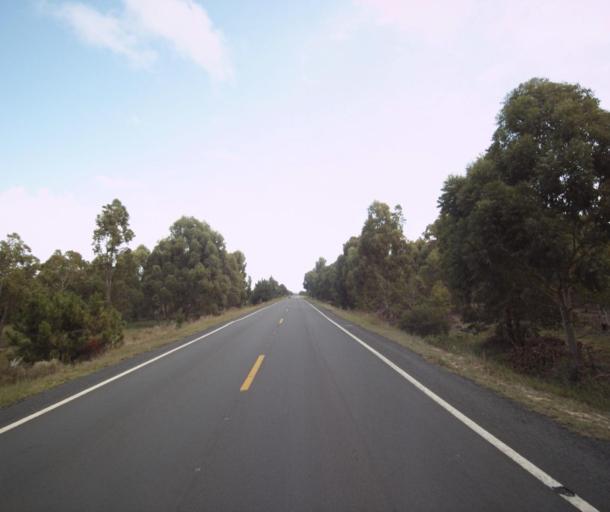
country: BR
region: Rio Grande do Sul
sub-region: Tapes
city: Tapes
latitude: -31.4303
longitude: -51.1886
